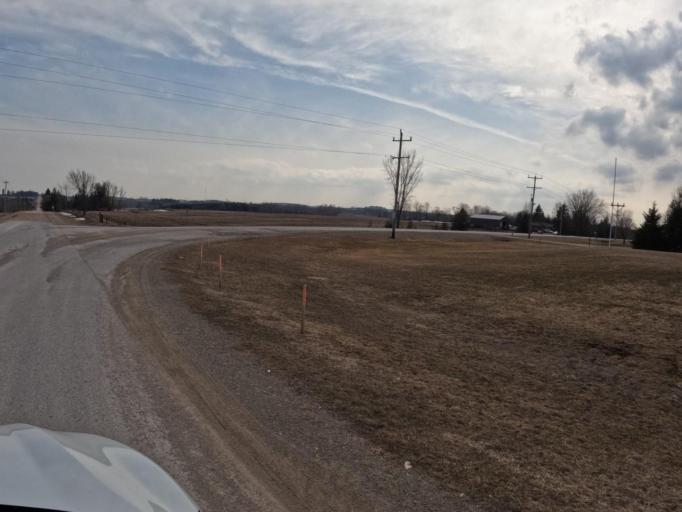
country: CA
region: Ontario
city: Shelburne
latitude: 43.9024
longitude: -80.3018
